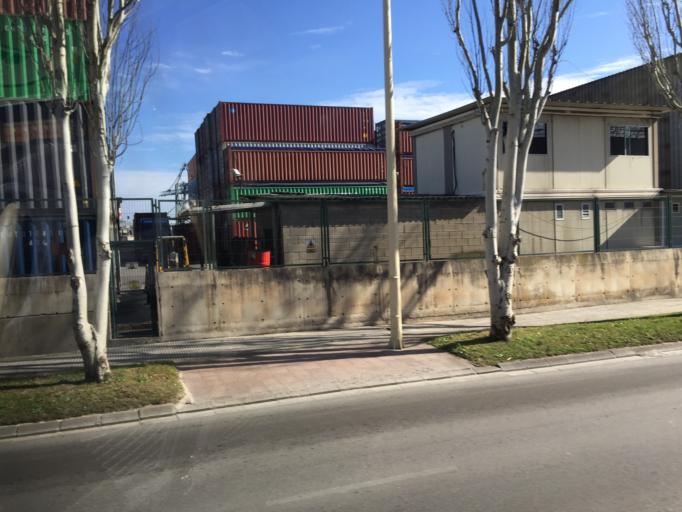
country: ES
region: Catalonia
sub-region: Provincia de Barcelona
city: Sants-Montjuic
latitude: 41.3416
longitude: 2.1444
